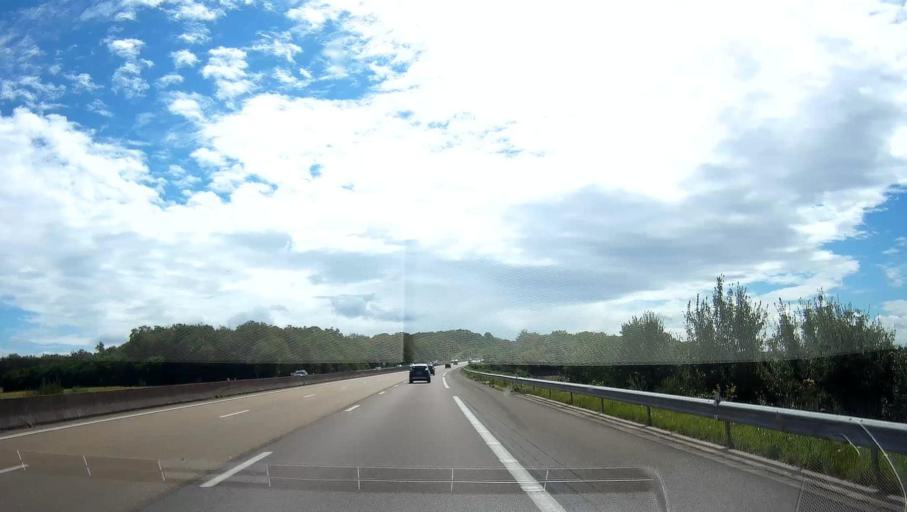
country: FR
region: Bourgogne
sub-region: Departement de la Cote-d'Or
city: Marcilly-sur-Tille
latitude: 47.4742
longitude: 5.1885
